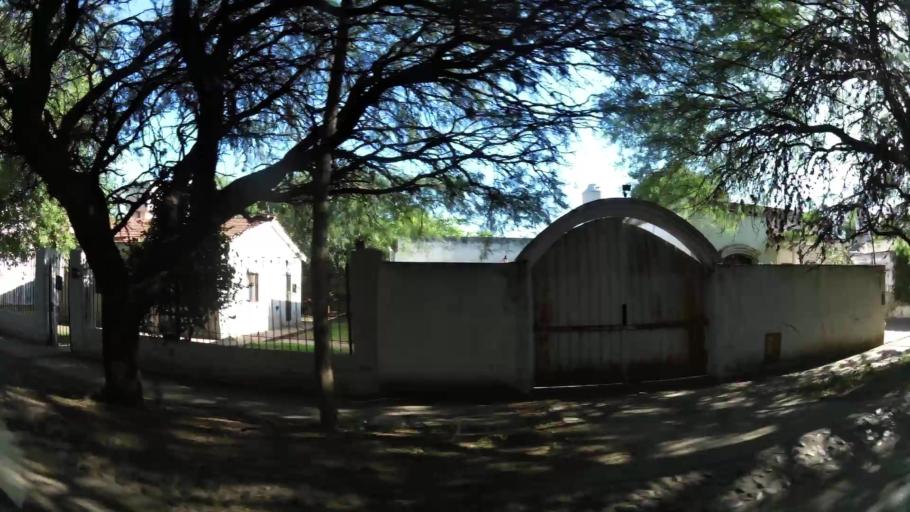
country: AR
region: Cordoba
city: Villa Allende
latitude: -31.3558
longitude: -64.2485
